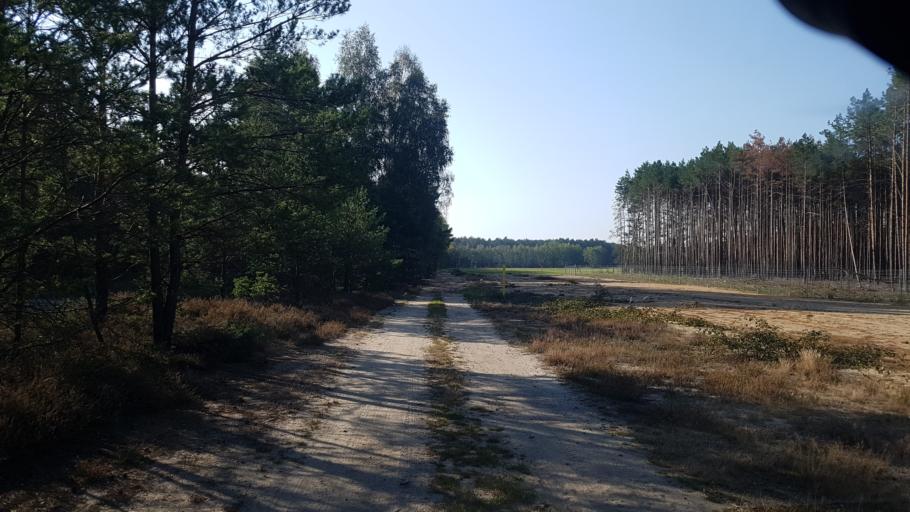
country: DE
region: Brandenburg
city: Finsterwalde
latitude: 51.6505
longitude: 13.6699
